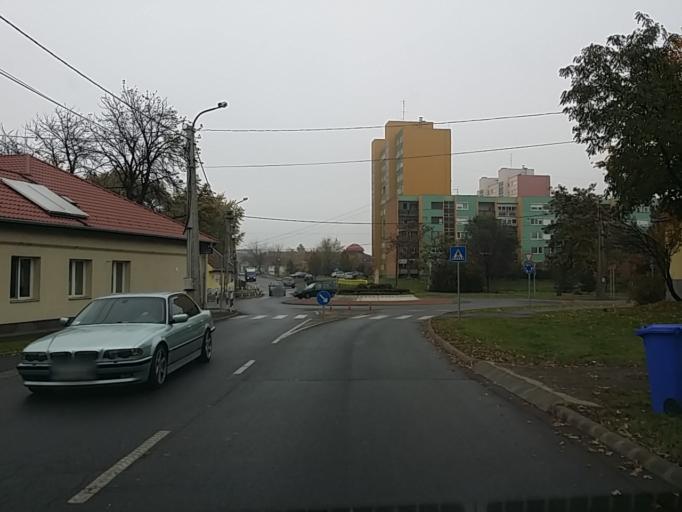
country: HU
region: Heves
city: Gyongyos
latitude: 47.7782
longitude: 19.9191
